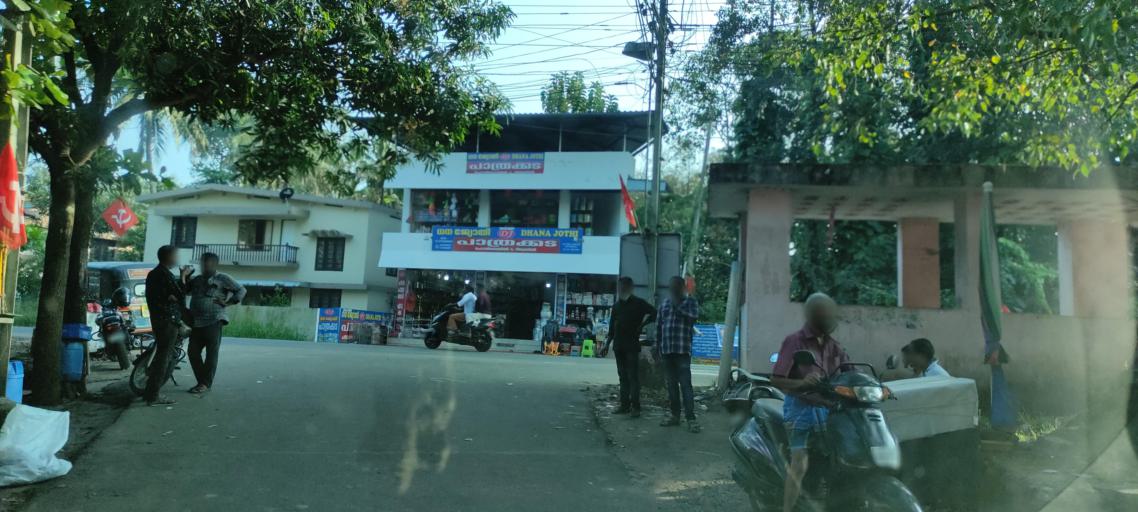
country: IN
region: Kerala
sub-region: Pattanamtitta
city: Adur
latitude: 9.1503
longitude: 76.7534
